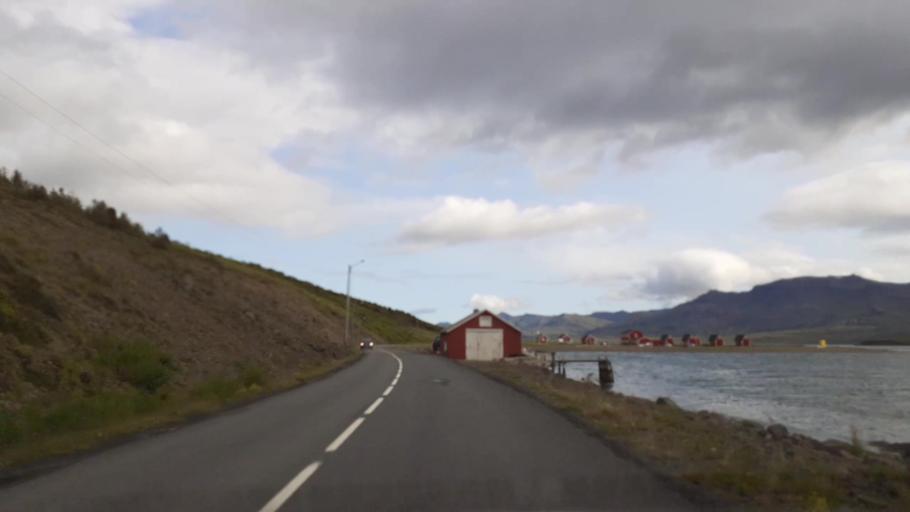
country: IS
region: East
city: Eskifjoerdur
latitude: 65.0632
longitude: -13.9954
